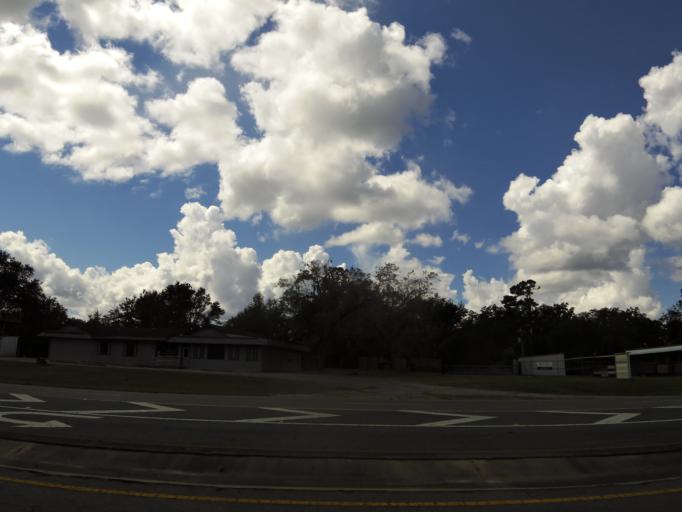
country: US
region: Georgia
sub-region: Charlton County
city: Folkston
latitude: 30.8098
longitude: -81.9971
